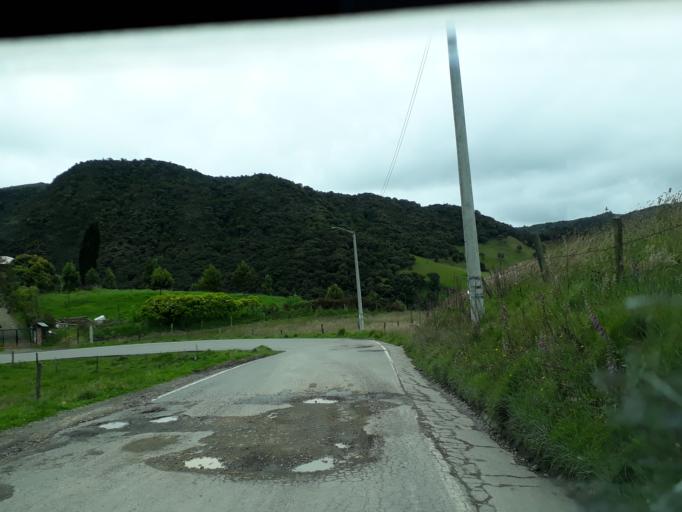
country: CO
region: Cundinamarca
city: Sutatausa
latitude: 5.1942
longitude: -73.8968
